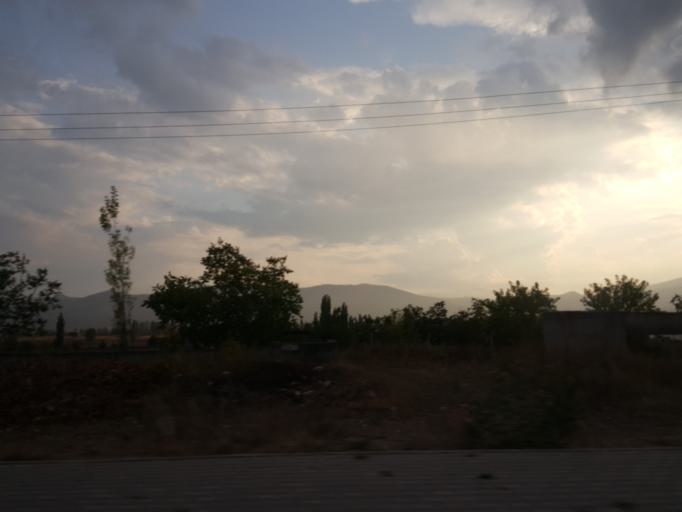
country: TR
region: Amasya
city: Gumushacikoy
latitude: 40.8762
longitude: 35.2339
